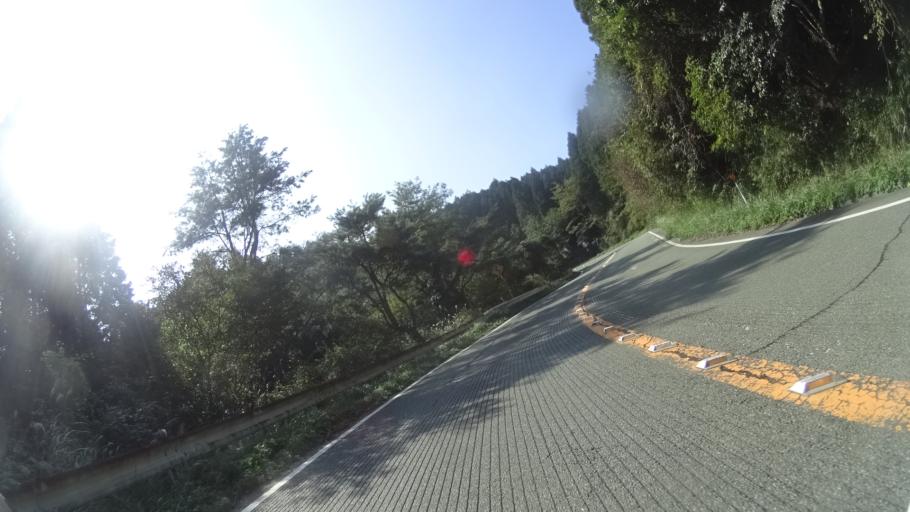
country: JP
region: Kumamoto
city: Aso
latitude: 32.9205
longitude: 130.9675
